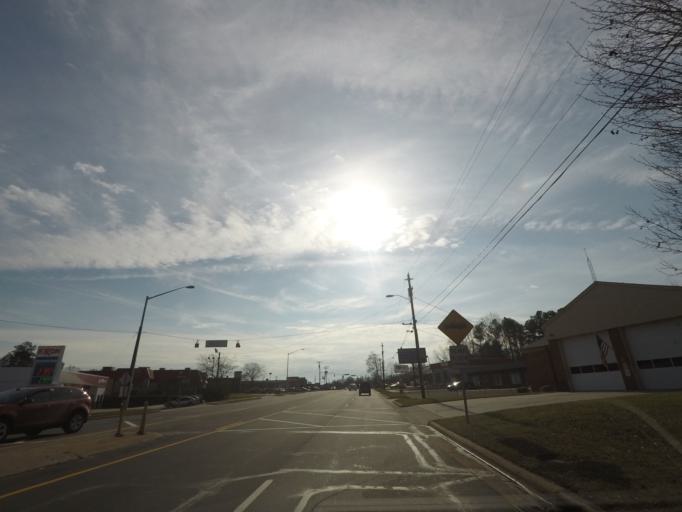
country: US
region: North Carolina
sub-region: Durham County
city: Durham
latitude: 36.0546
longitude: -78.9040
